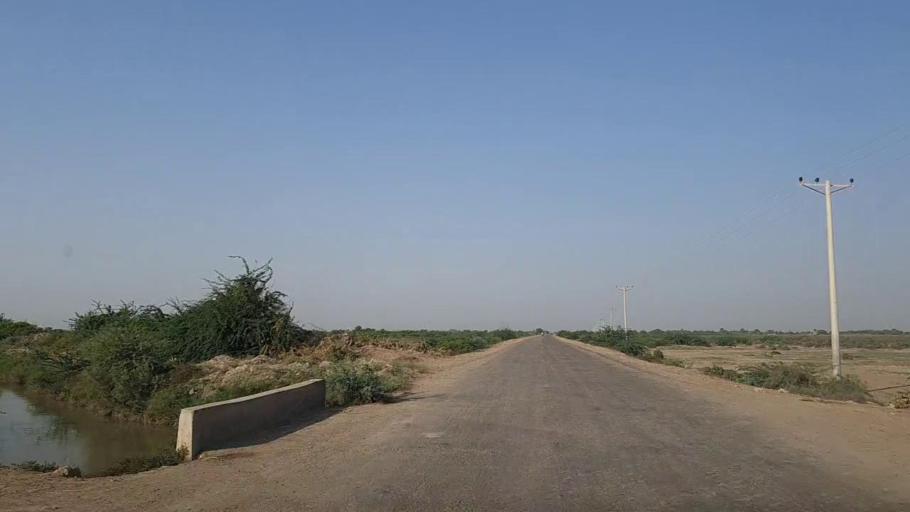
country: PK
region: Sindh
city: Mirpur Batoro
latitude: 24.6138
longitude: 68.4043
